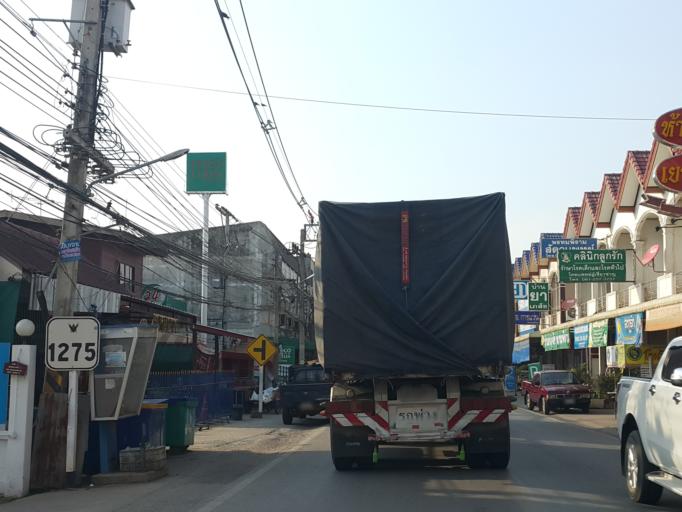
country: TH
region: Phitsanulok
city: Phrom Phiram
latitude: 17.0335
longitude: 100.1997
